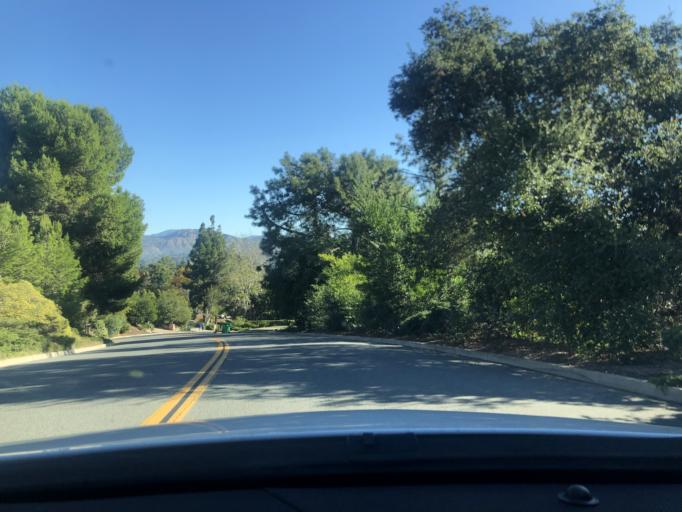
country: US
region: California
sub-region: San Diego County
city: Rancho San Diego
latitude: 32.7694
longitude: -116.9432
